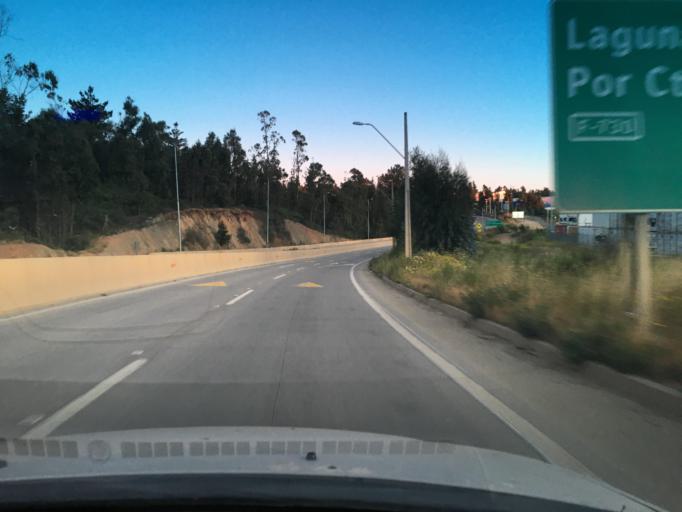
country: CL
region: Valparaiso
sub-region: Provincia de Valparaiso
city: Valparaiso
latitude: -33.0924
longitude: -71.6046
